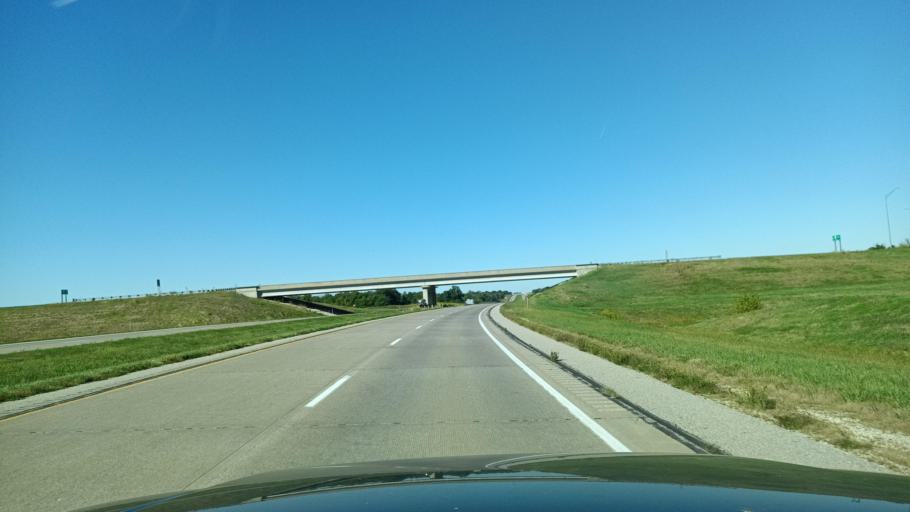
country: US
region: Iowa
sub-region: Lee County
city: Fort Madison
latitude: 40.6709
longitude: -91.2702
